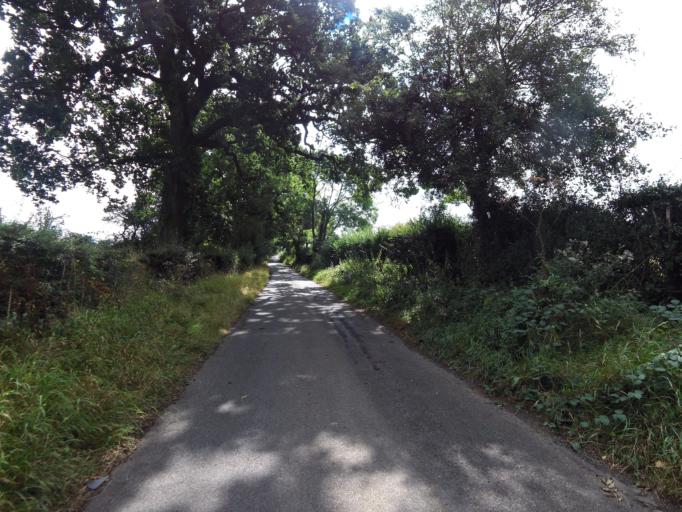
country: GB
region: England
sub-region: Hertfordshire
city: Shenley AV
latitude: 51.6929
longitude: -0.2469
